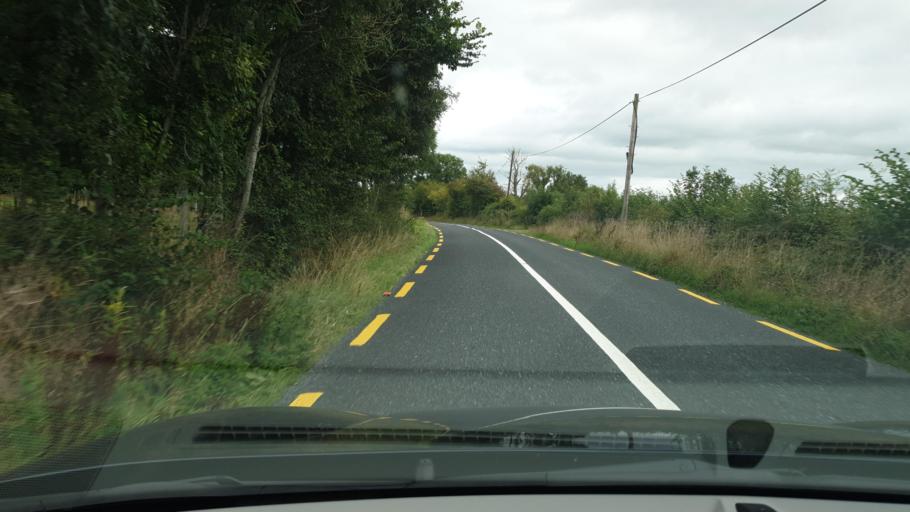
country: IE
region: Leinster
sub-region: Kildare
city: Naas
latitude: 53.2269
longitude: -6.7066
